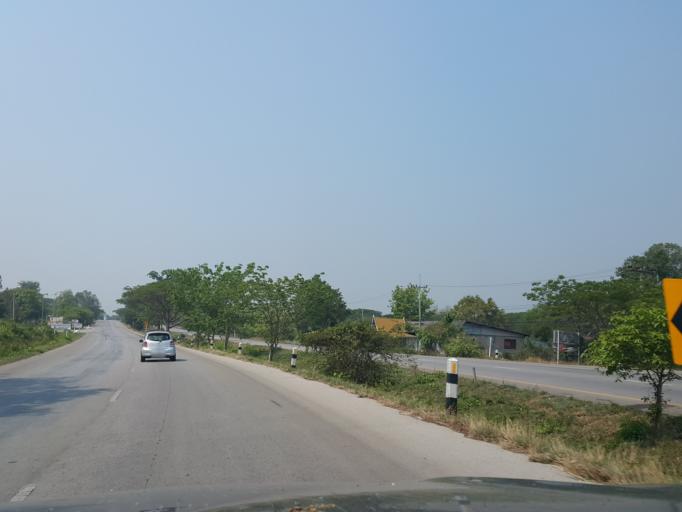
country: TH
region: Lampang
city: Sop Prap
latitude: 17.9389
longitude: 99.3486
